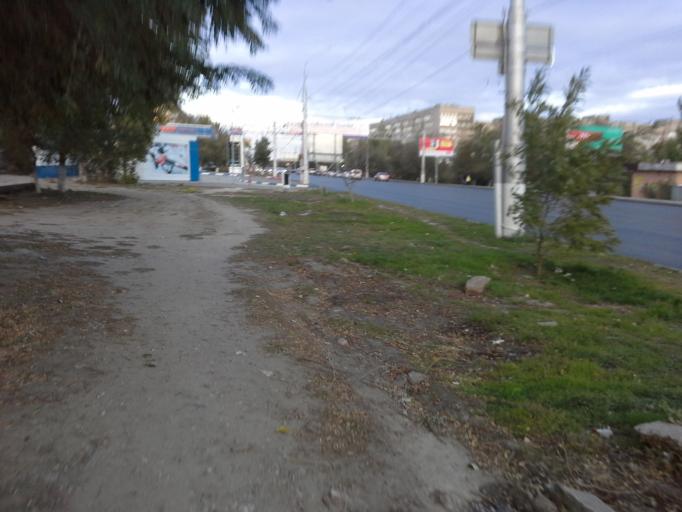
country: RU
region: Volgograd
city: Vodstroy
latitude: 48.8203
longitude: 44.6336
